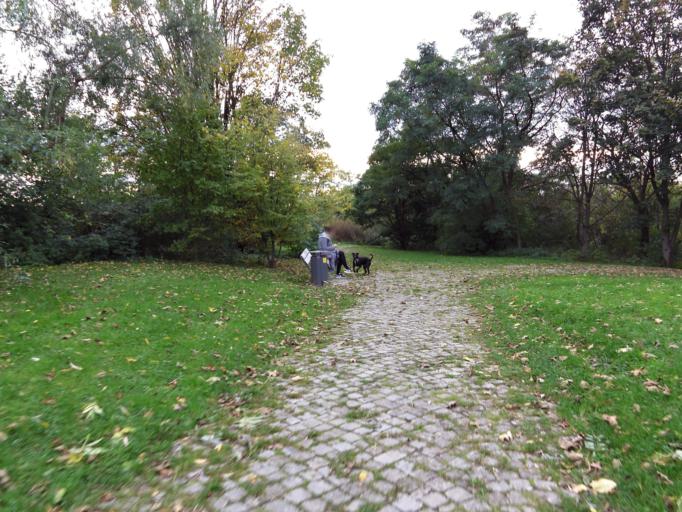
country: DE
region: Saxony
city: Leipzig
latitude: 51.3082
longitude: 12.4250
